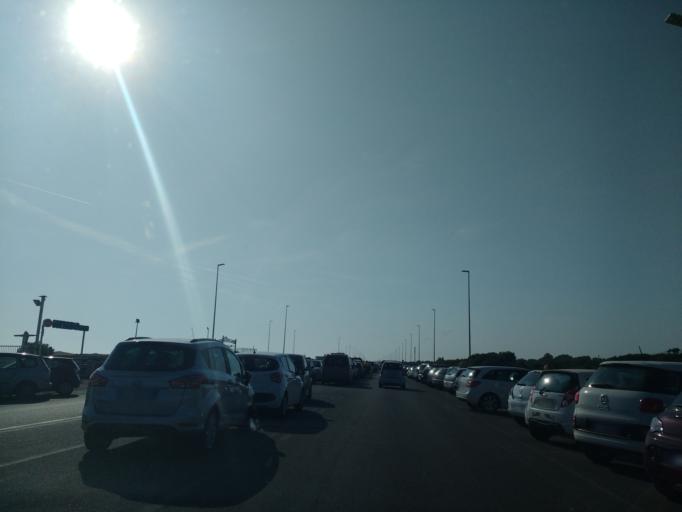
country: IT
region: Latium
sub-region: Citta metropolitana di Roma Capitale
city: Acilia-Castel Fusano-Ostia Antica
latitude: 41.7034
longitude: 12.3425
